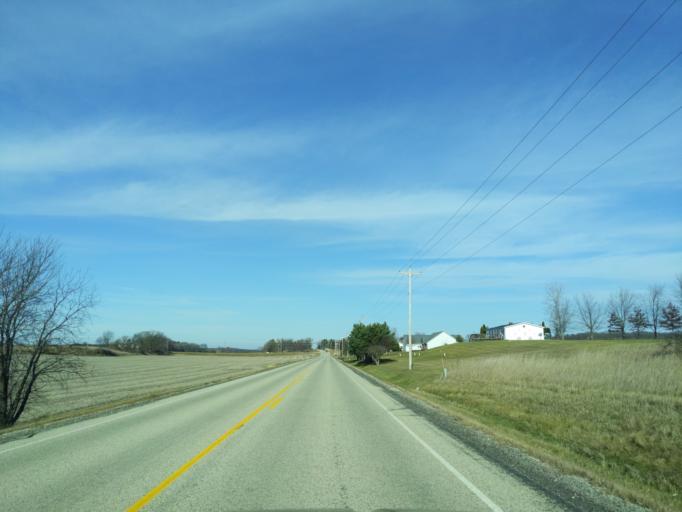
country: US
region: Wisconsin
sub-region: Jefferson County
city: Palmyra
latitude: 42.7797
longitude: -88.6026
